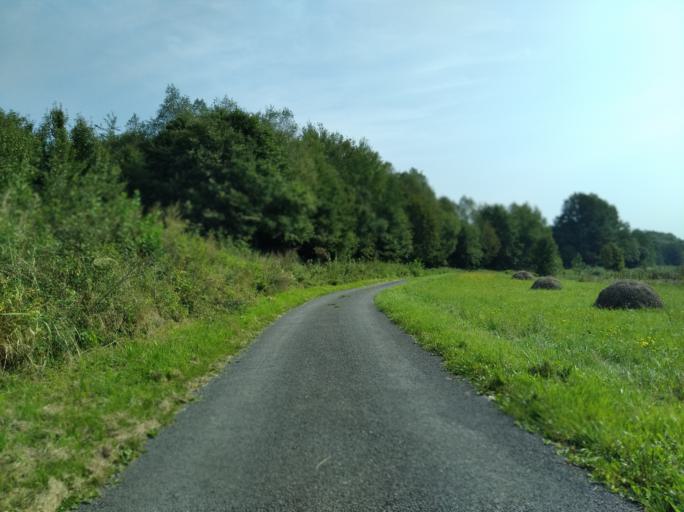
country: PL
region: Subcarpathian Voivodeship
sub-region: Powiat przeworski
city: Jawornik Polski
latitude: 49.8907
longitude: 22.2594
